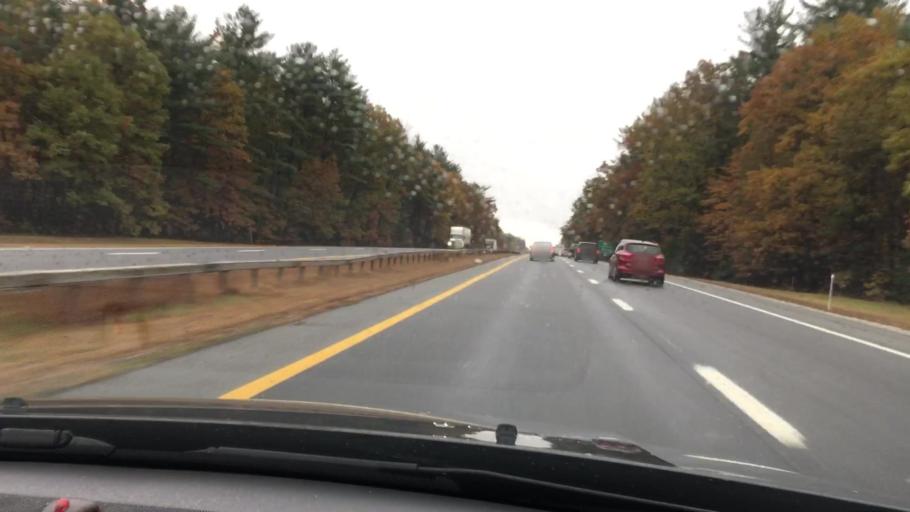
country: US
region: New Hampshire
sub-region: Hillsborough County
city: Litchfield
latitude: 42.8015
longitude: -71.4983
